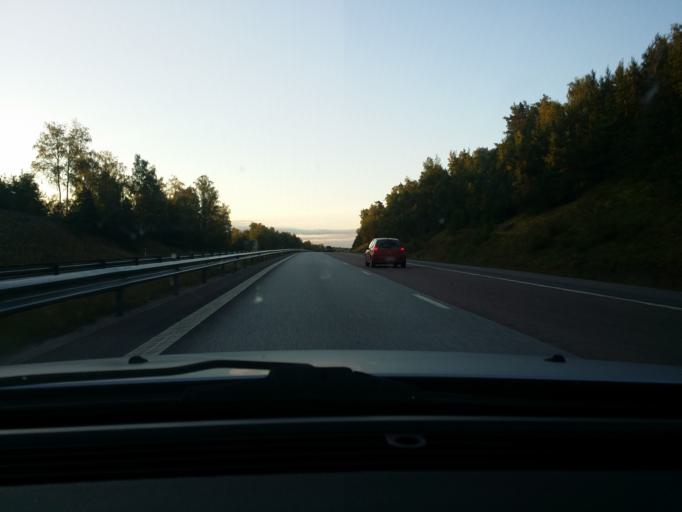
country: SE
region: Uppsala
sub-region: Habo Kommun
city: Balsta
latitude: 59.5809
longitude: 17.5282
